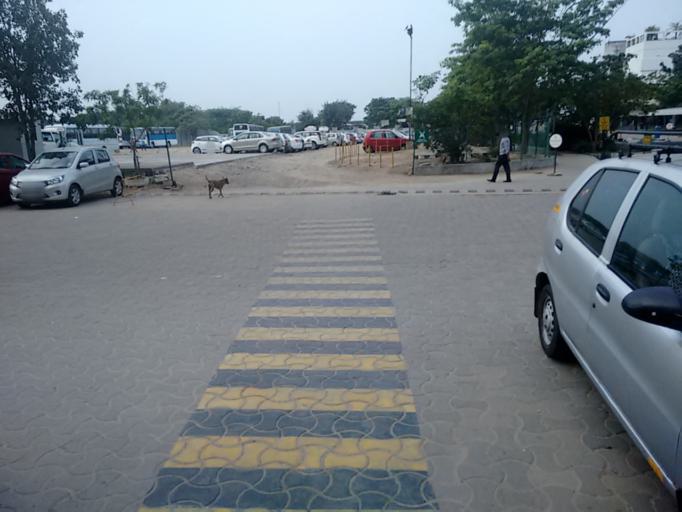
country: IN
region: Tamil Nadu
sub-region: Kancheepuram
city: Perungudi
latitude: 12.9484
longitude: 80.2320
